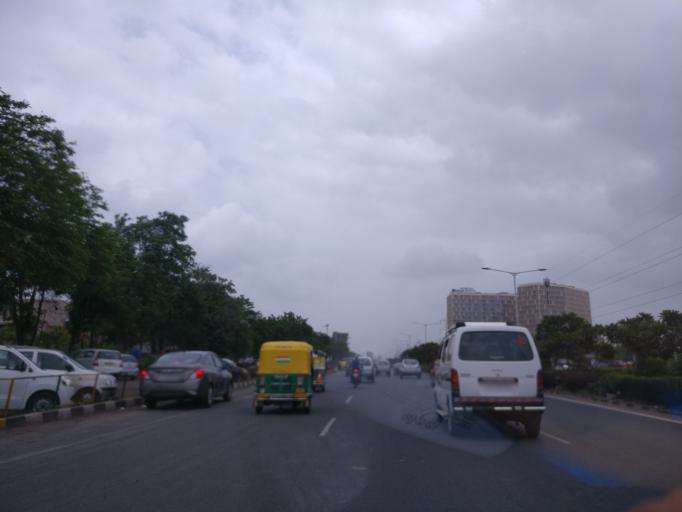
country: IN
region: Gujarat
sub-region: Ahmadabad
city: Sarkhej
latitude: 23.0192
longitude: 72.5048
